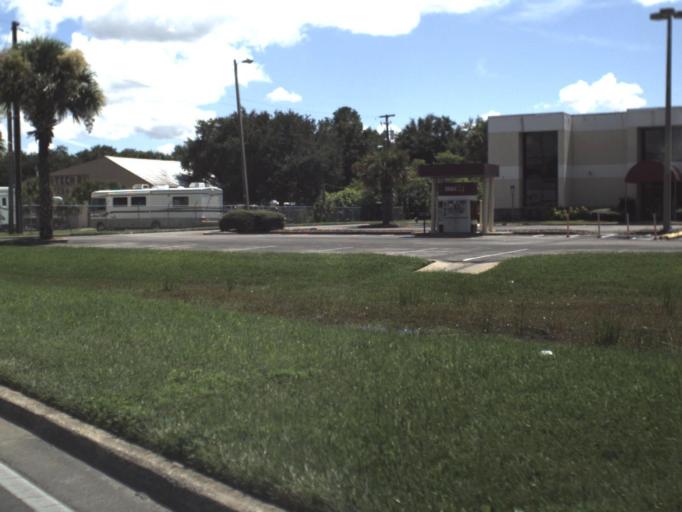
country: US
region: Florida
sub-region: Polk County
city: Inwood
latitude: 28.0523
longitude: -81.7733
